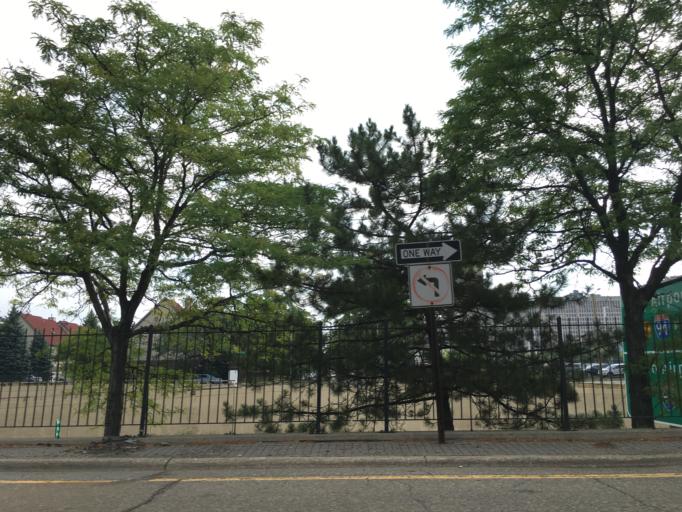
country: US
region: Michigan
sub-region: Wayne County
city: Highland Park
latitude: 42.3683
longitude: -83.0832
